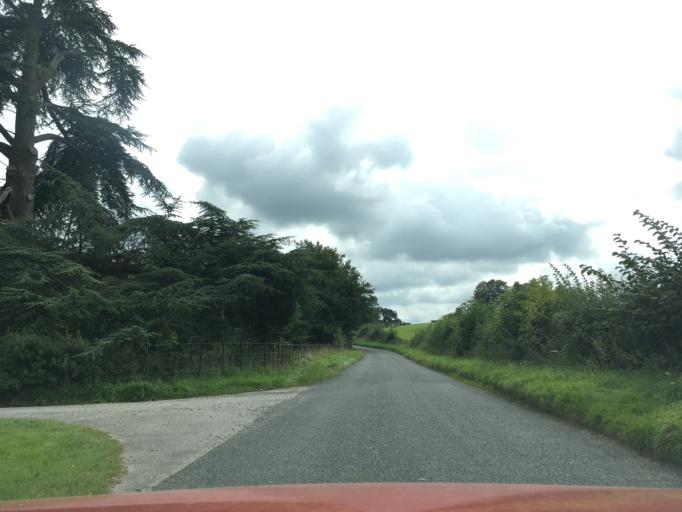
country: GB
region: England
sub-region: South Gloucestershire
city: Charfield
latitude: 51.6383
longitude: -2.4300
